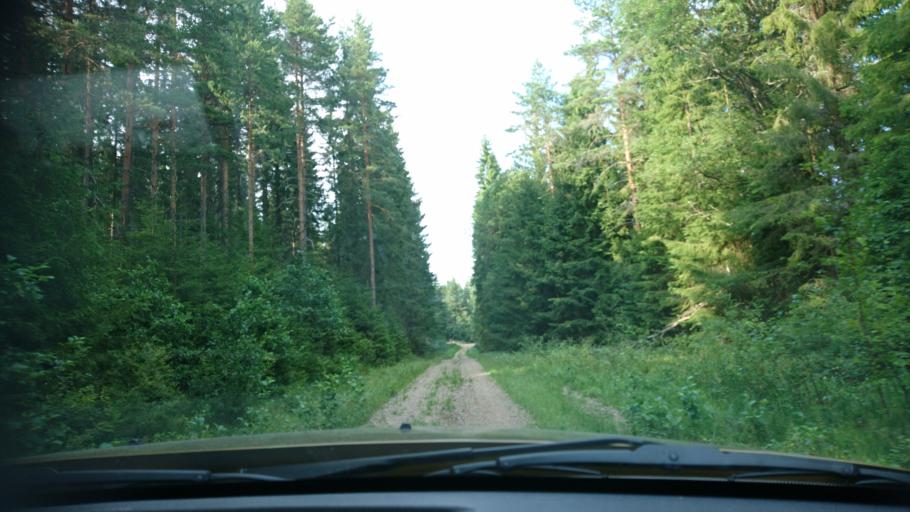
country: SE
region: Vaermland
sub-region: Kristinehamns Kommun
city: Bjorneborg
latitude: 59.3003
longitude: 14.3083
